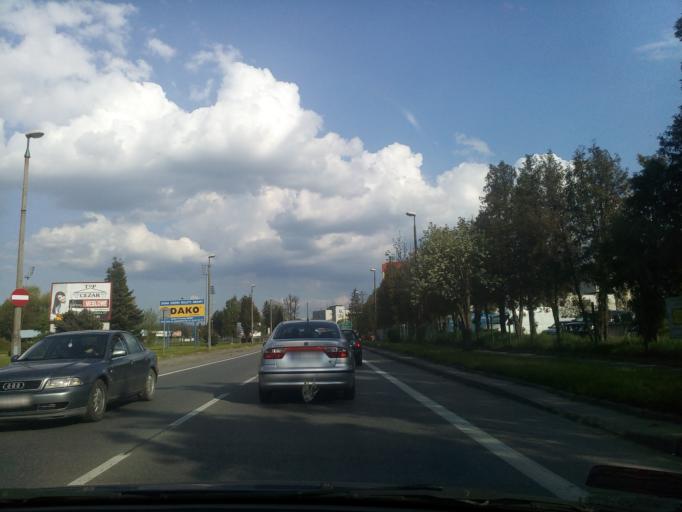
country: PL
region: Lesser Poland Voivodeship
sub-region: Powiat nowosadecki
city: Nowy Sacz
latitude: 49.6221
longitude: 20.6988
